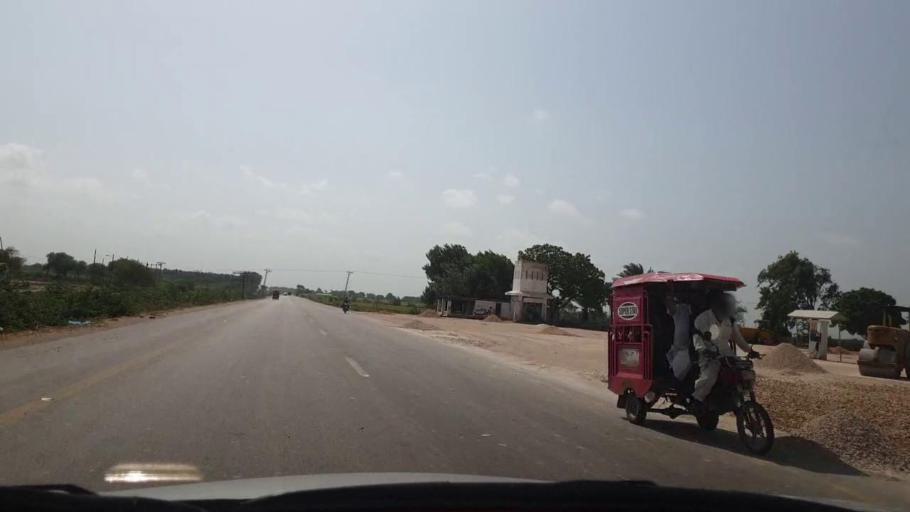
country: PK
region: Sindh
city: Matli
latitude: 24.9912
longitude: 68.6575
